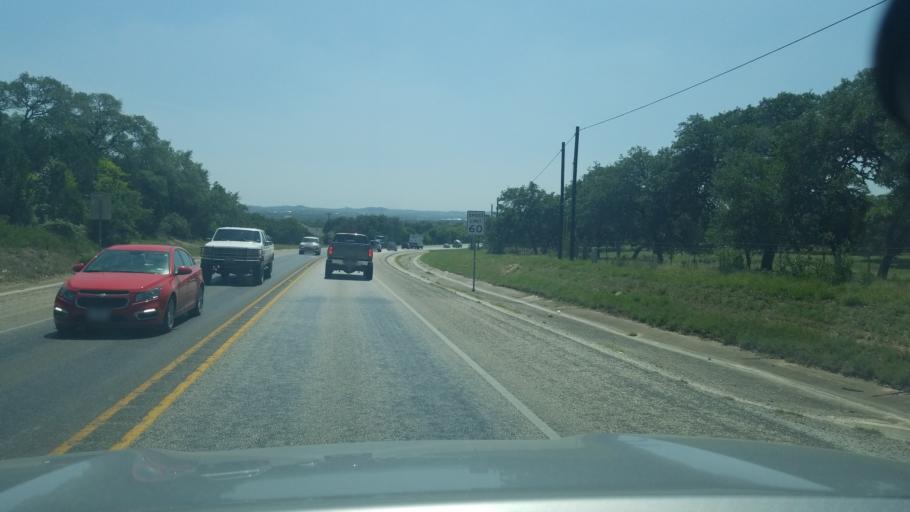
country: US
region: Texas
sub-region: Kendall County
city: Boerne
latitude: 29.7880
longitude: -98.6874
